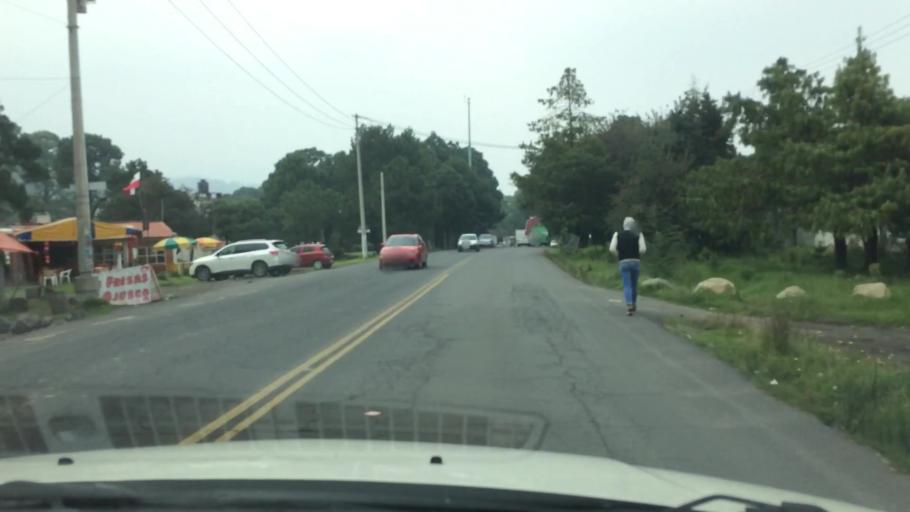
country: MX
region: Mexico City
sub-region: Tlalpan
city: Lomas de Tepemecatl
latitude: 19.2440
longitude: -99.2408
